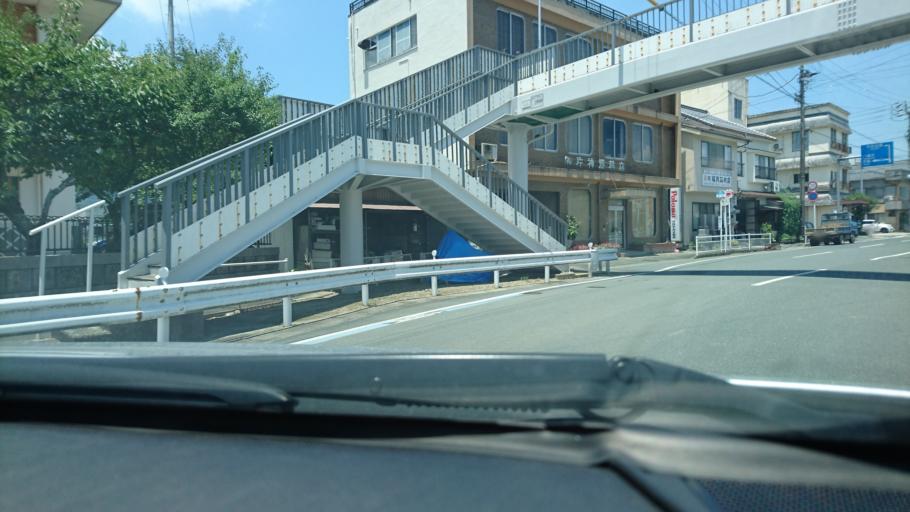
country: JP
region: Ehime
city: Ozu
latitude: 33.5069
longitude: 132.5427
